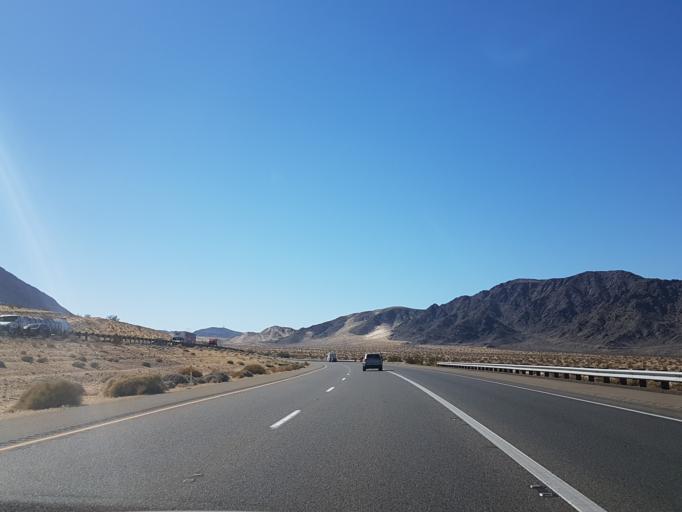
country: US
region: California
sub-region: San Bernardino County
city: Fort Irwin
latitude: 35.0987
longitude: -116.2911
